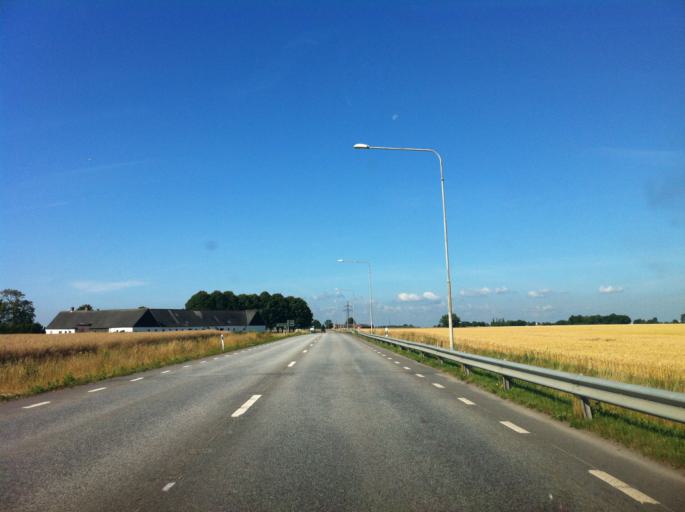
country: SE
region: Skane
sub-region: Landskrona
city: Asmundtorp
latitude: 55.8844
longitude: 12.9067
